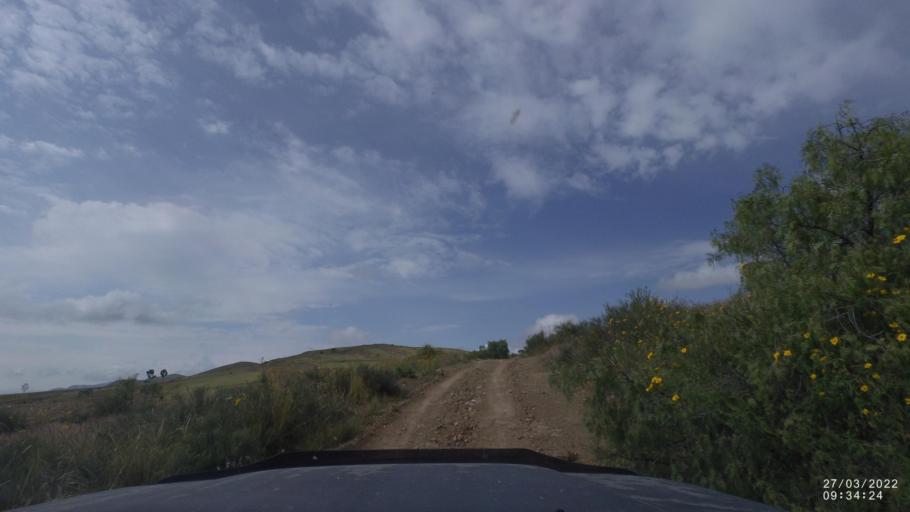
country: BO
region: Cochabamba
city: Cliza
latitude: -17.7423
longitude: -65.8910
